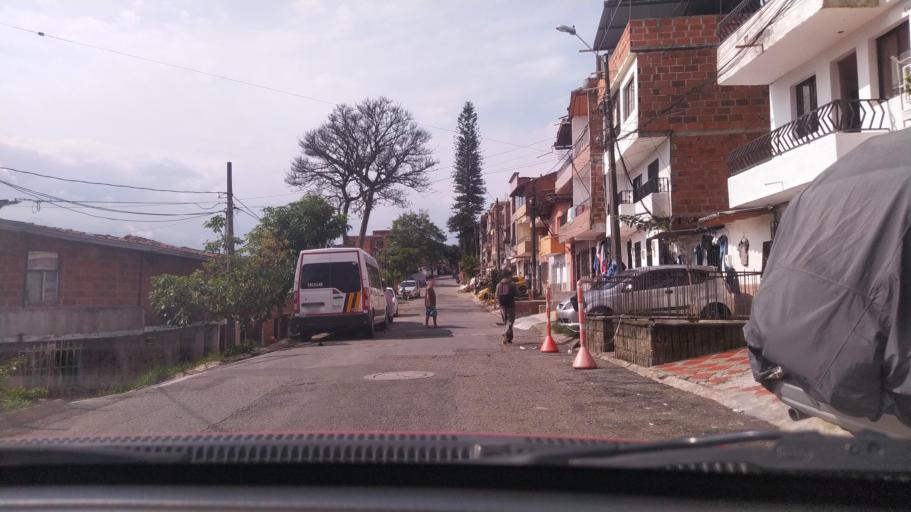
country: CO
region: Antioquia
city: Medellin
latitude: 6.2636
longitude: -75.5490
